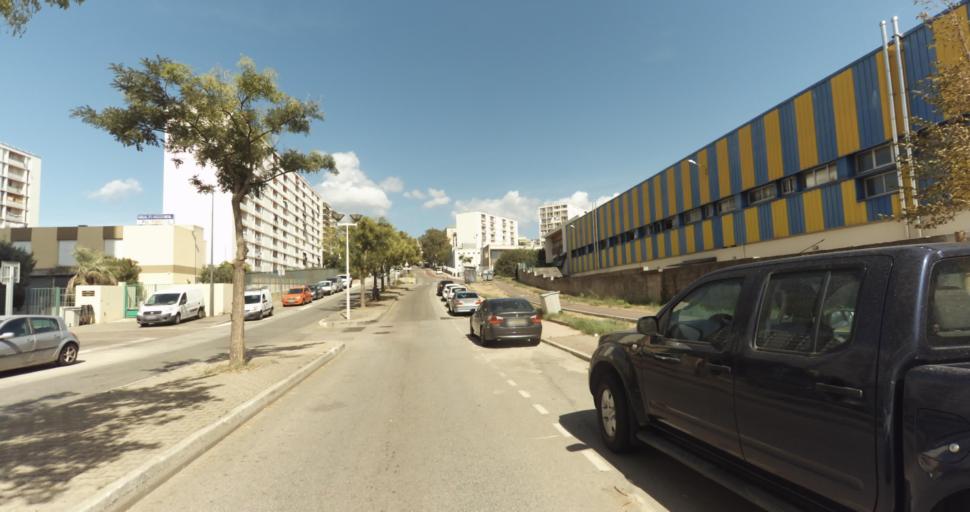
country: FR
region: Corsica
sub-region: Departement de la Corse-du-Sud
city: Ajaccio
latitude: 41.9368
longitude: 8.7509
